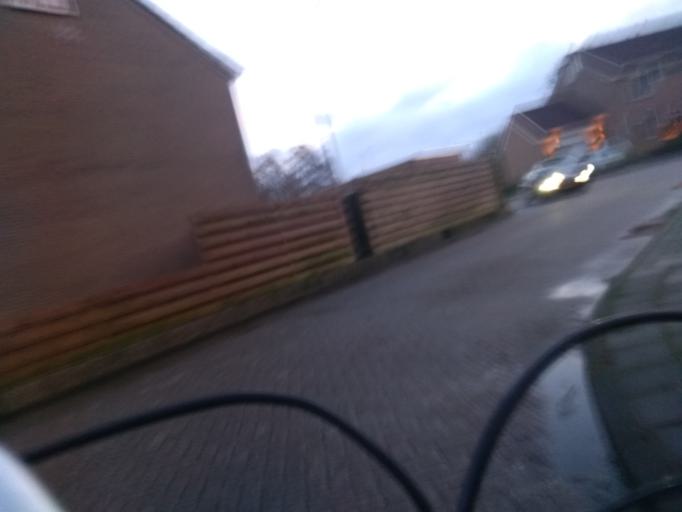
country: NL
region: Drenthe
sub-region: Gemeente Assen
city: Assen
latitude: 53.0185
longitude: 6.5619
